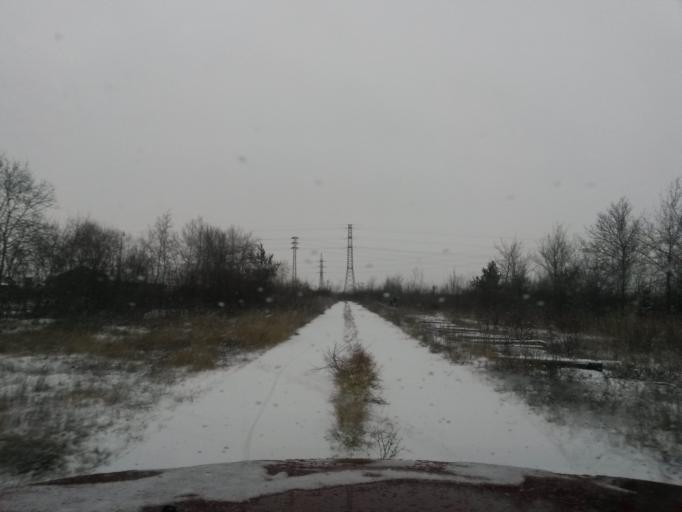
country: SK
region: Kosicky
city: Moldava nad Bodvou
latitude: 48.5986
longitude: 21.0041
